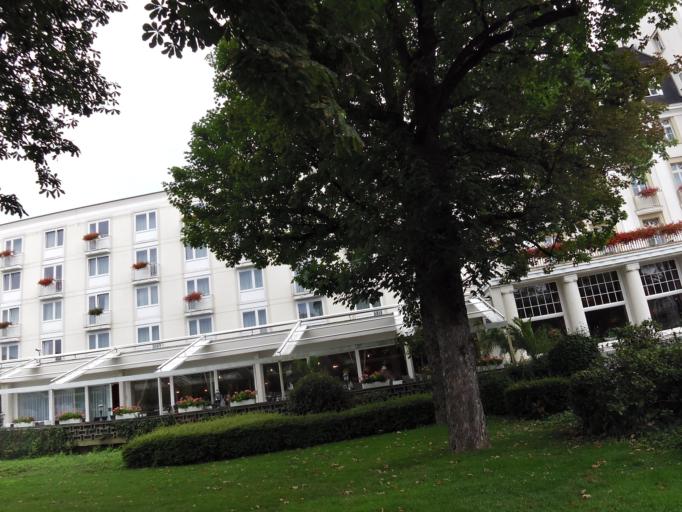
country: DE
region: Rheinland-Pfalz
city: Bad Neuenahr-Ahrweiler
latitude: 50.5424
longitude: 7.1375
